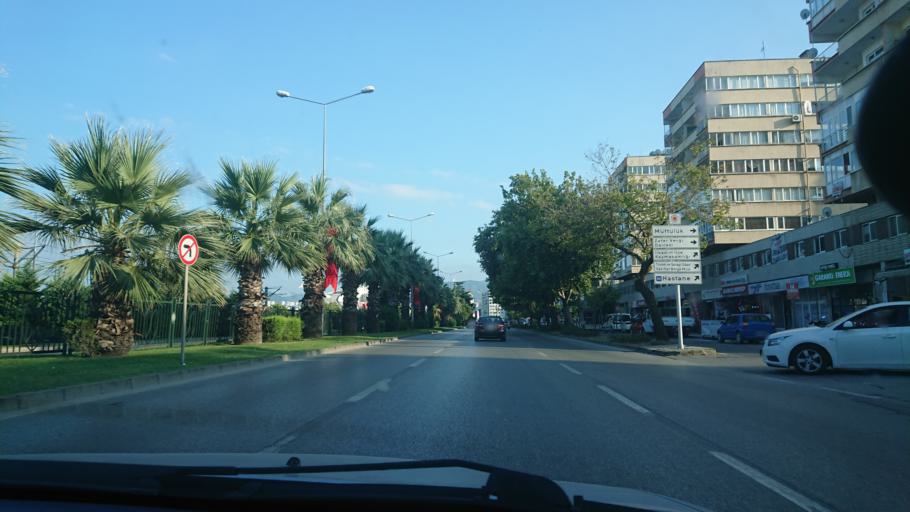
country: TR
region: Samsun
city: Samsun
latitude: 41.2988
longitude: 36.3322
